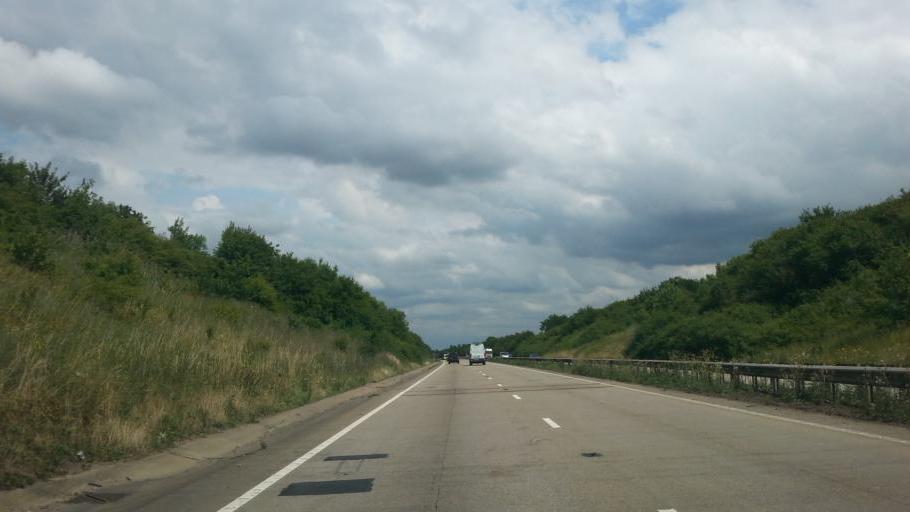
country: GB
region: England
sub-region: Norfolk
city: Hingham
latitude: 52.5385
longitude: 1.0736
